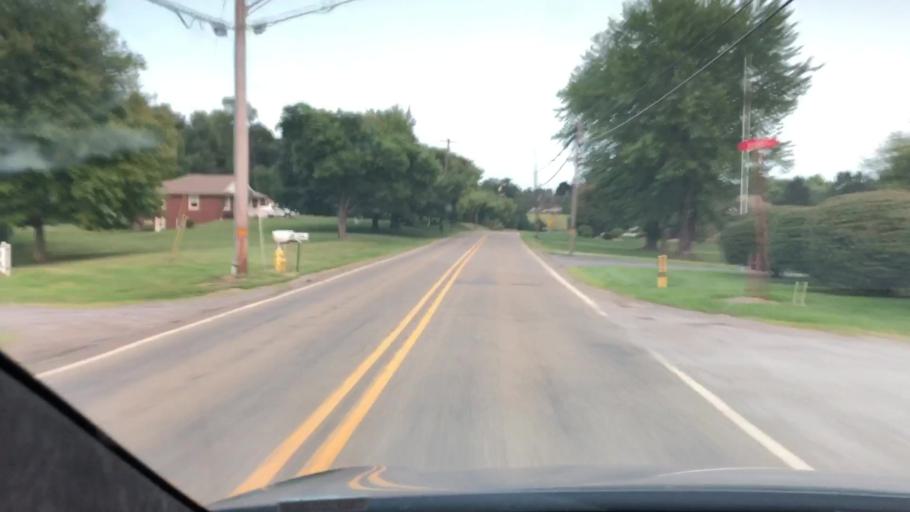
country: US
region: Pennsylvania
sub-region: Butler County
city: Homeacre-Lyndora
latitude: 40.8845
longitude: -79.9195
